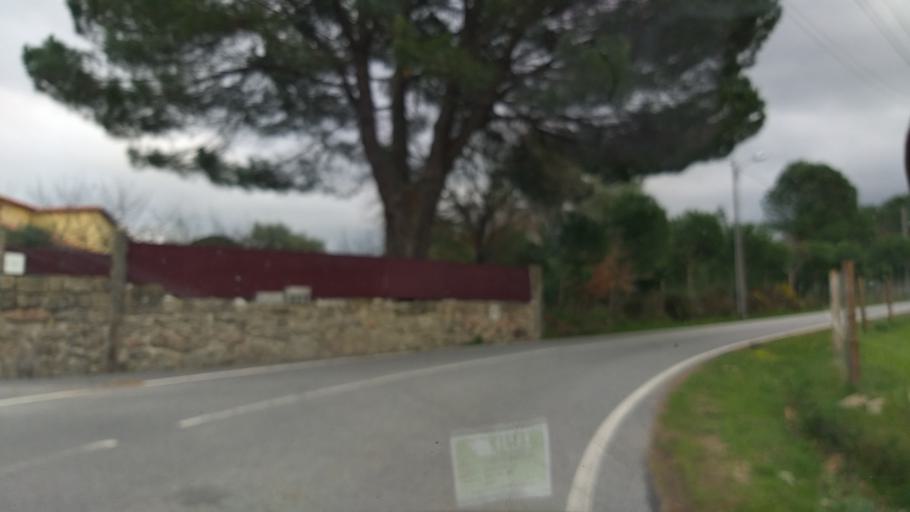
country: PT
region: Guarda
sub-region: Seia
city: Seia
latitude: 40.4740
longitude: -7.6434
